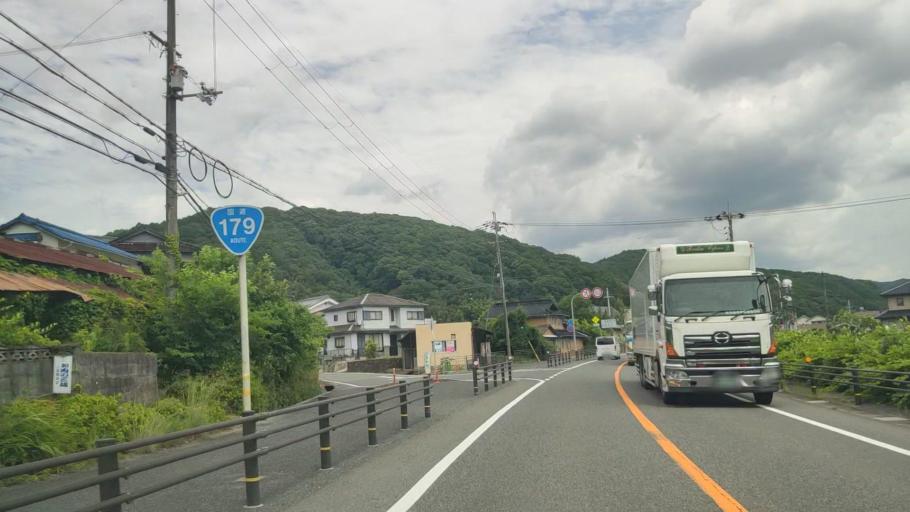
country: JP
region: Hyogo
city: Yamazakicho-nakabirose
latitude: 34.9868
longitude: 134.4323
